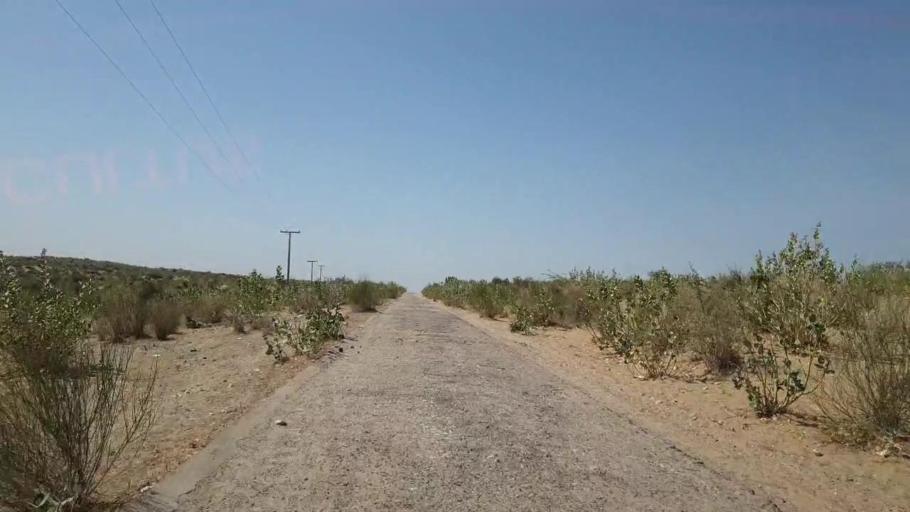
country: PK
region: Sindh
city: Umarkot
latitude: 25.1625
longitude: 69.9593
